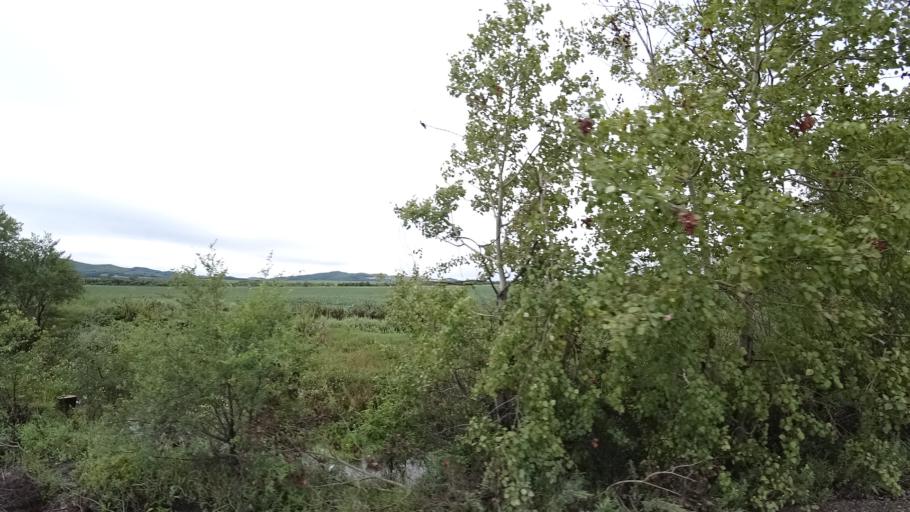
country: RU
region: Primorskiy
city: Monastyrishche
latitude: 44.1820
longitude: 132.4840
